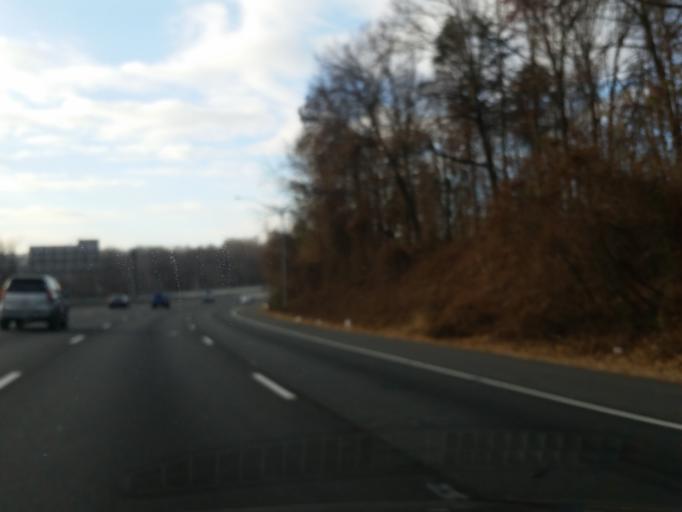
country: US
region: Maryland
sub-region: Montgomery County
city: Cabin John
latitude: 38.9872
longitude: -77.1573
